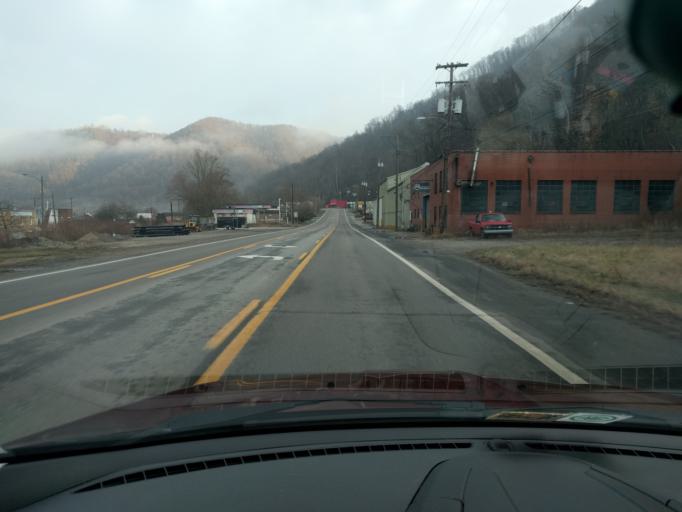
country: US
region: West Virginia
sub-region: Kanawha County
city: Montgomery
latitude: 38.1735
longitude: -81.3038
